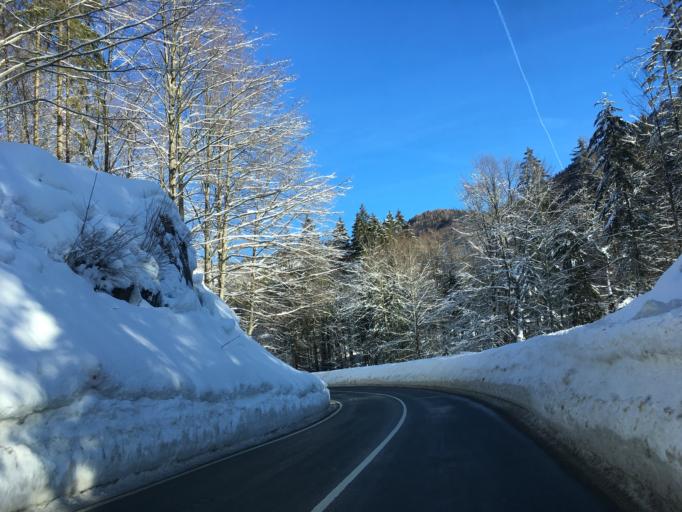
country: DE
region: Bavaria
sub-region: Upper Bavaria
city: Aschau im Chiemgau
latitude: 47.7231
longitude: 12.2935
